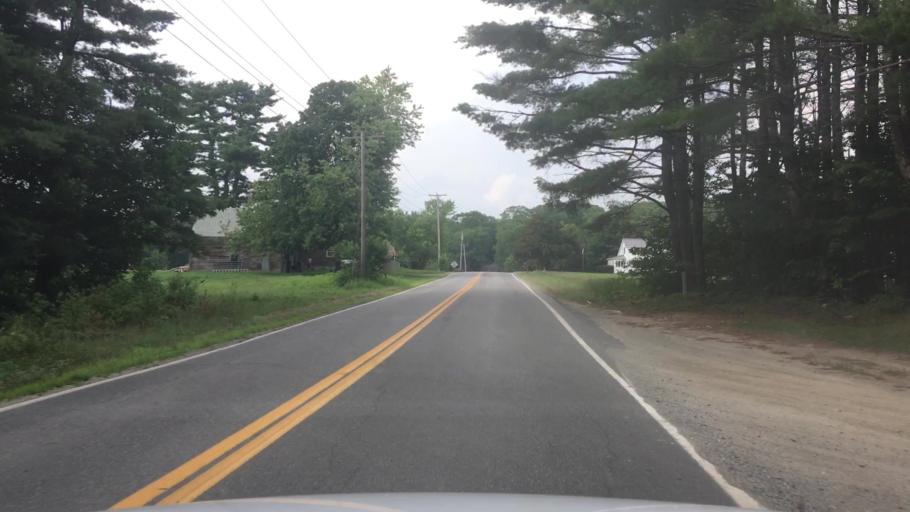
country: US
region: Maine
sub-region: Knox County
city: Washington
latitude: 44.2290
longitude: -69.3880
